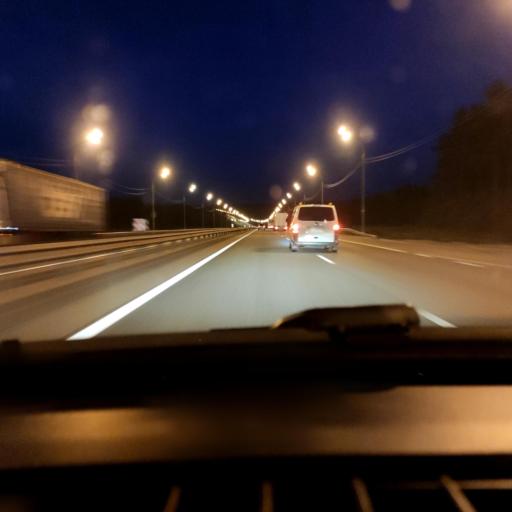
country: RU
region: Lipetsk
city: Khlevnoye
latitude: 52.2297
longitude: 39.0933
